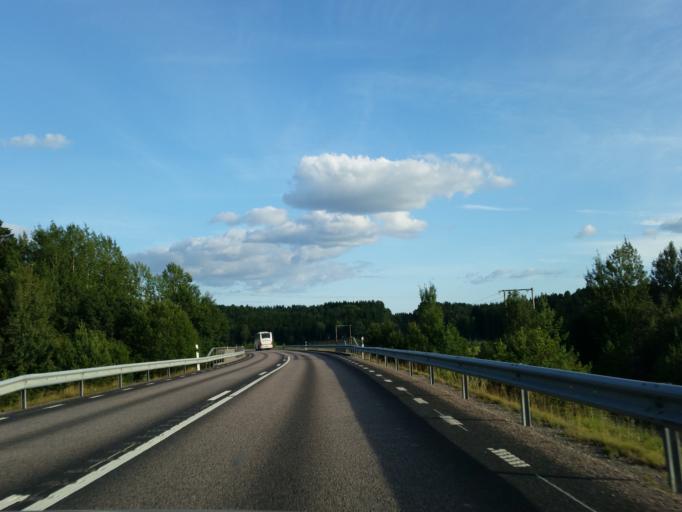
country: SE
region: Soedermanland
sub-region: Gnesta Kommun
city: Gnesta
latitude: 59.0412
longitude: 17.2939
